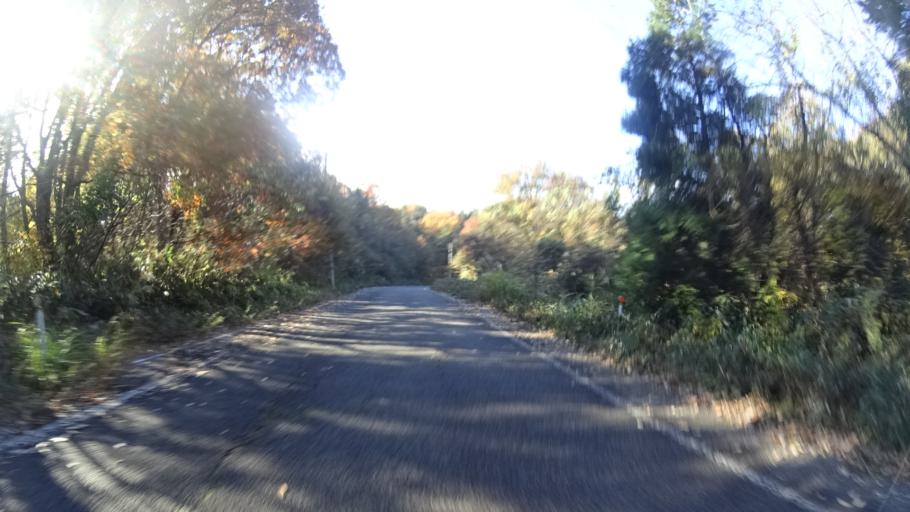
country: JP
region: Niigata
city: Yoshida-kasugacho
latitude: 37.6576
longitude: 138.8132
